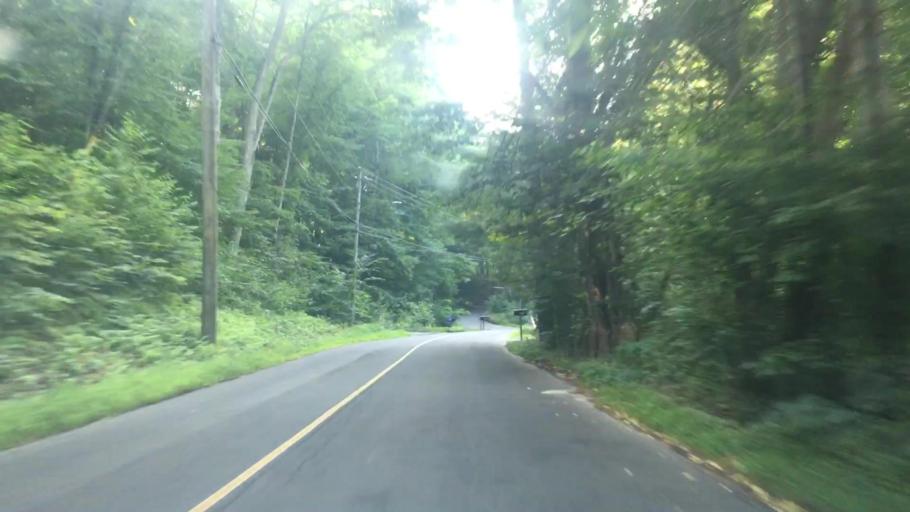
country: US
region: Connecticut
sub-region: Middlesex County
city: Chester Center
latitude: 41.3956
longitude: -72.4528
